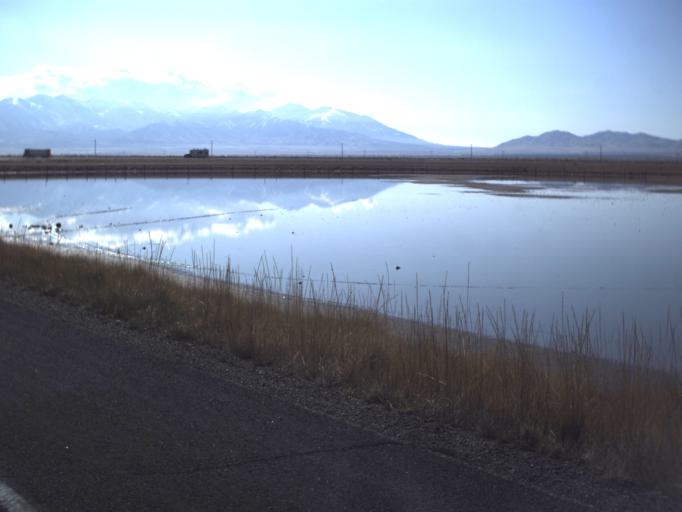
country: US
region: Utah
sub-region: Tooele County
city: Grantsville
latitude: 40.7102
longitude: -112.5250
